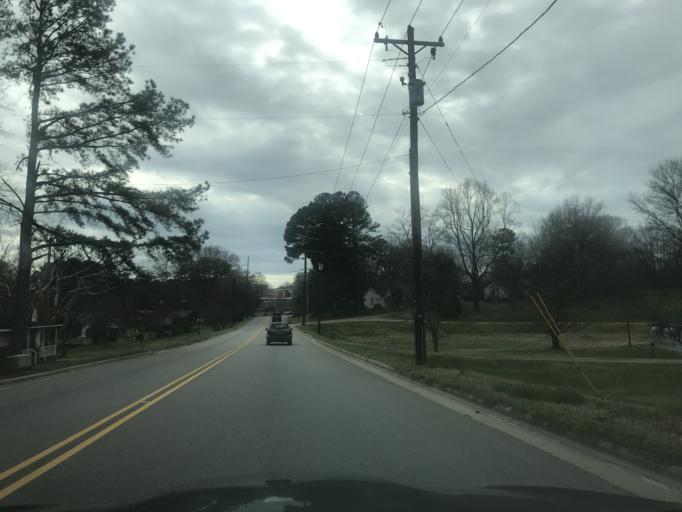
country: US
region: North Carolina
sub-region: Franklin County
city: Franklinton
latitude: 36.1017
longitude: -78.4528
